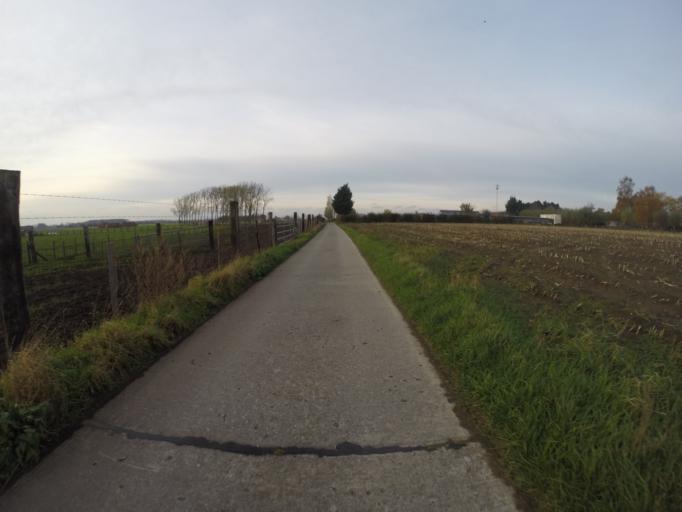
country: BE
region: Flanders
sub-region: Provincie Oost-Vlaanderen
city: Aalter
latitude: 51.0541
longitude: 3.4585
